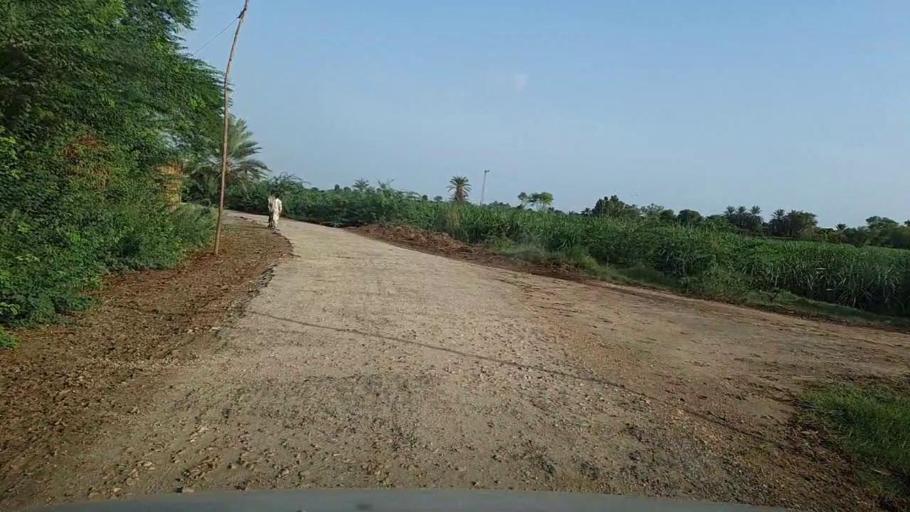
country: PK
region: Sindh
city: Pad Idan
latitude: 26.8076
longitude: 68.2351
